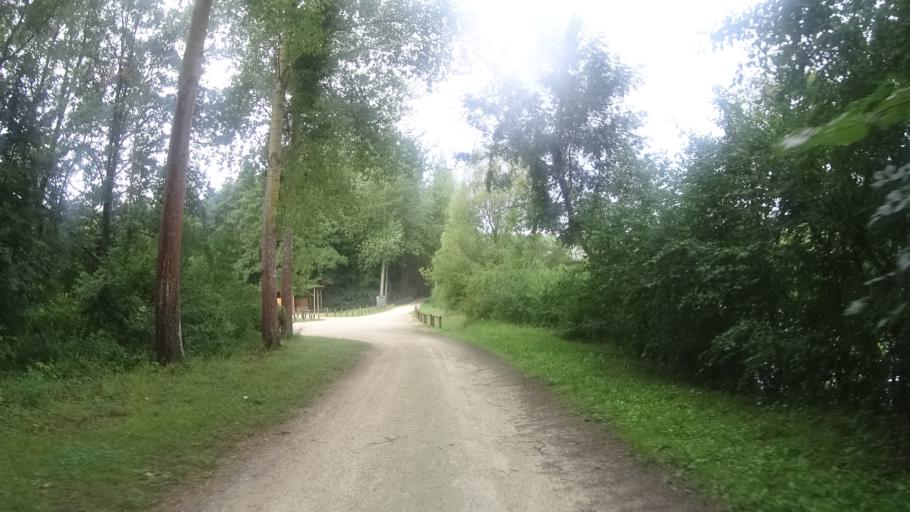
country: FR
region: Bourgogne
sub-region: Departement de l'Yonne
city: Joigny
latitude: 47.9572
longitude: 3.4155
